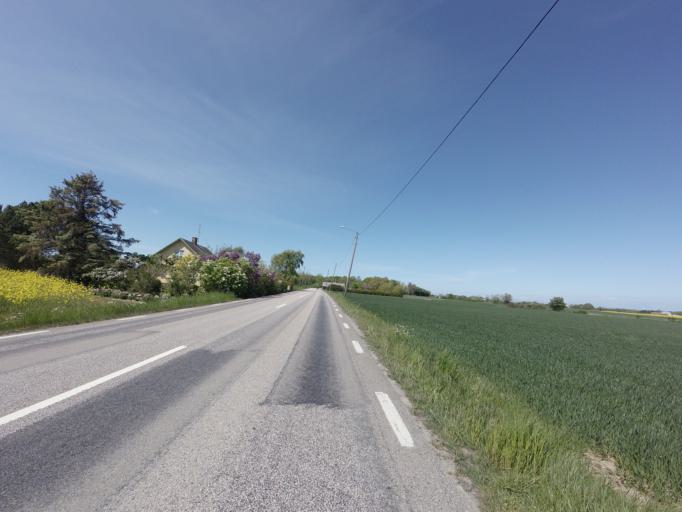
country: SE
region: Skane
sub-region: Helsingborg
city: Odakra
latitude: 56.1460
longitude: 12.6809
